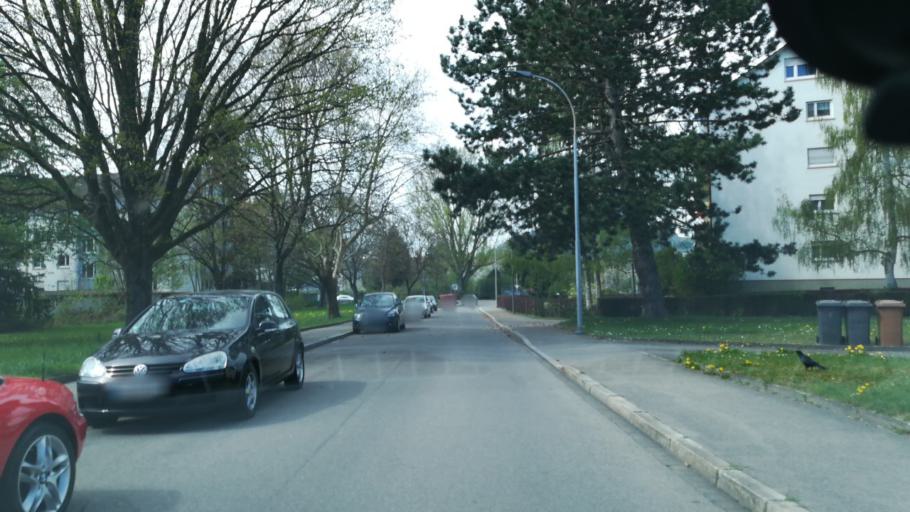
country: DE
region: Baden-Wuerttemberg
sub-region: Freiburg Region
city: Singen
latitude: 47.7712
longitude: 8.8446
